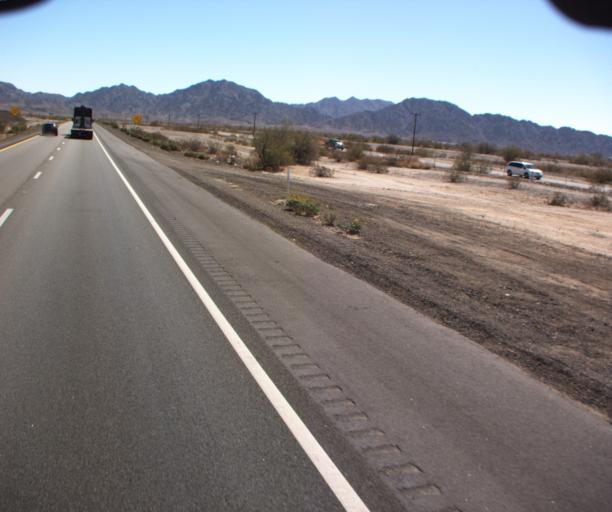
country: US
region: Arizona
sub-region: Yuma County
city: Fortuna Foothills
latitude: 32.6630
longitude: -114.3838
